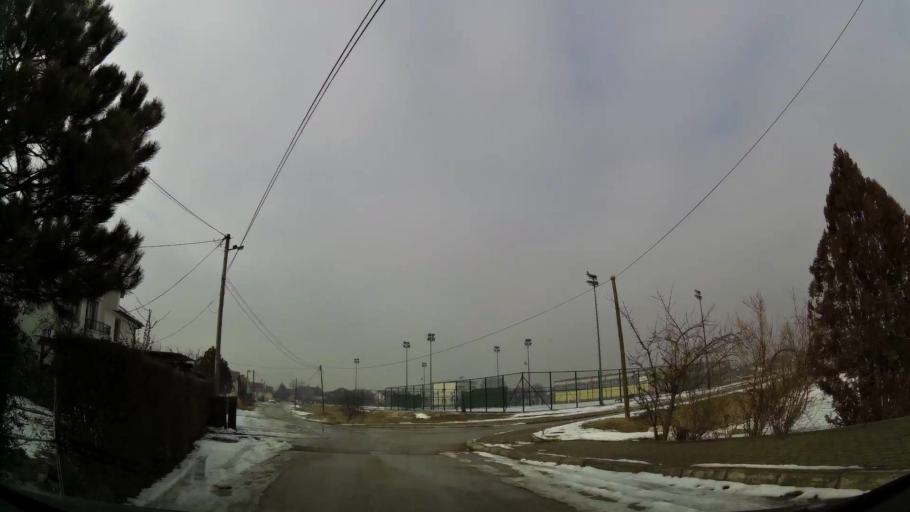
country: MK
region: Ilinden
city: Ilinden
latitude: 41.9893
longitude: 21.5830
